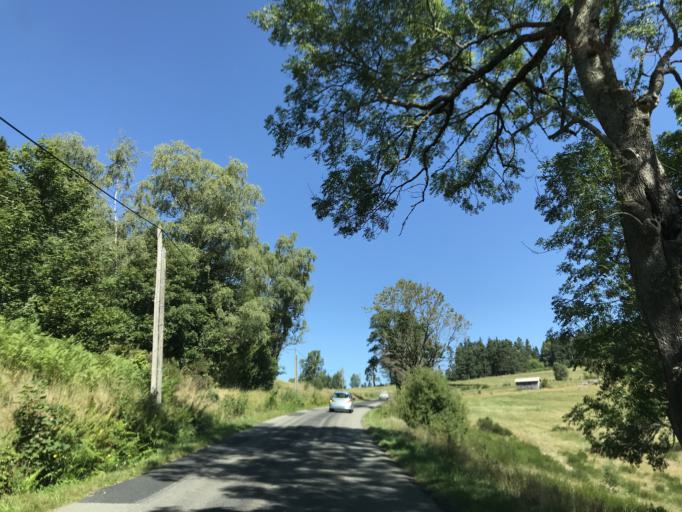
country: FR
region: Auvergne
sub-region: Departement du Puy-de-Dome
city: Job
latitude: 45.6768
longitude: 3.7476
